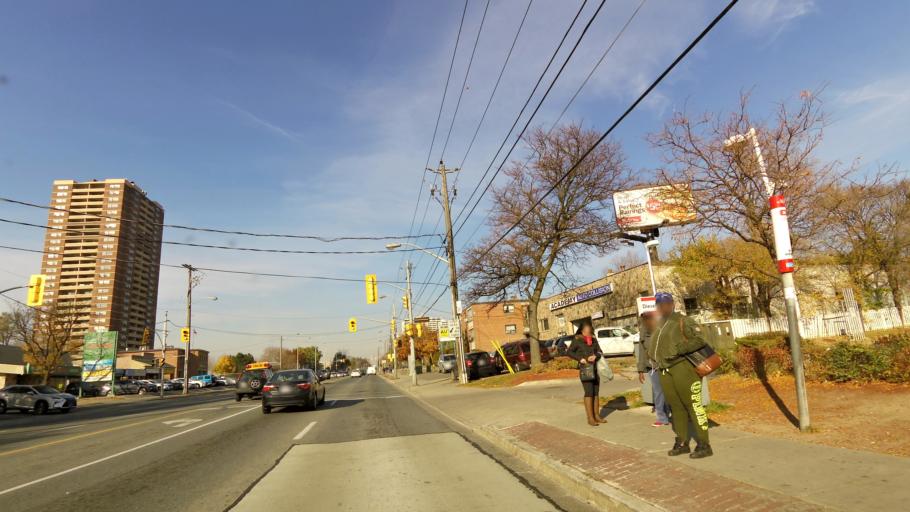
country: CA
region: Ontario
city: Concord
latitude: 43.7226
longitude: -79.5089
